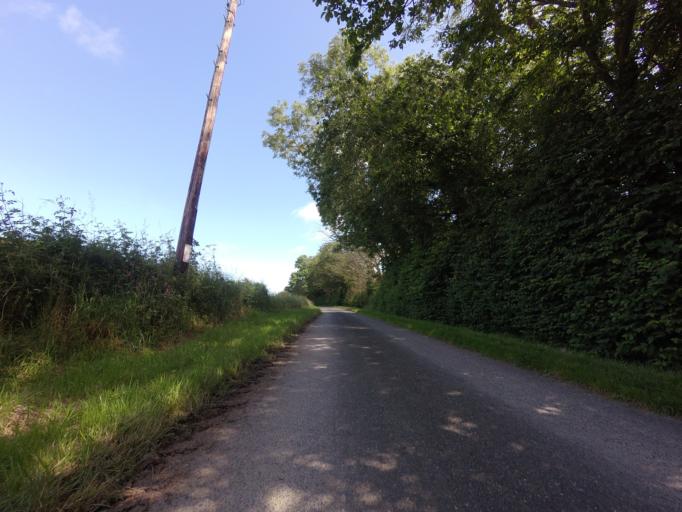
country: GB
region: Scotland
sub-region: Aberdeenshire
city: Banff
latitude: 57.6138
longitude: -2.5104
